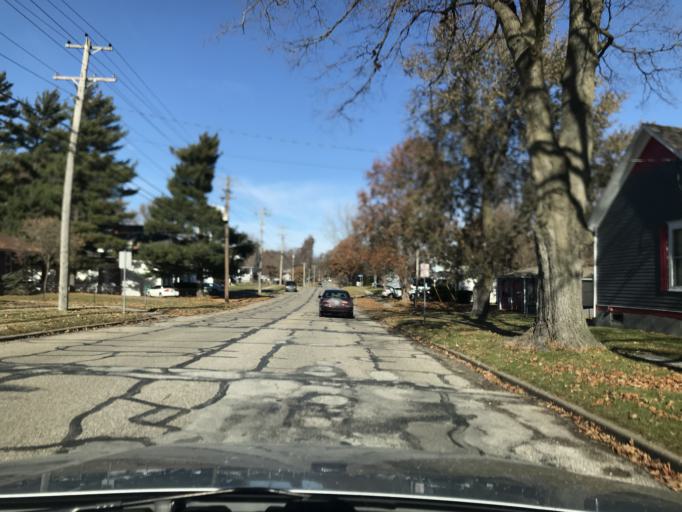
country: US
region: Illinois
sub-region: McDonough County
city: Macomb
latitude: 40.4498
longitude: -90.6673
